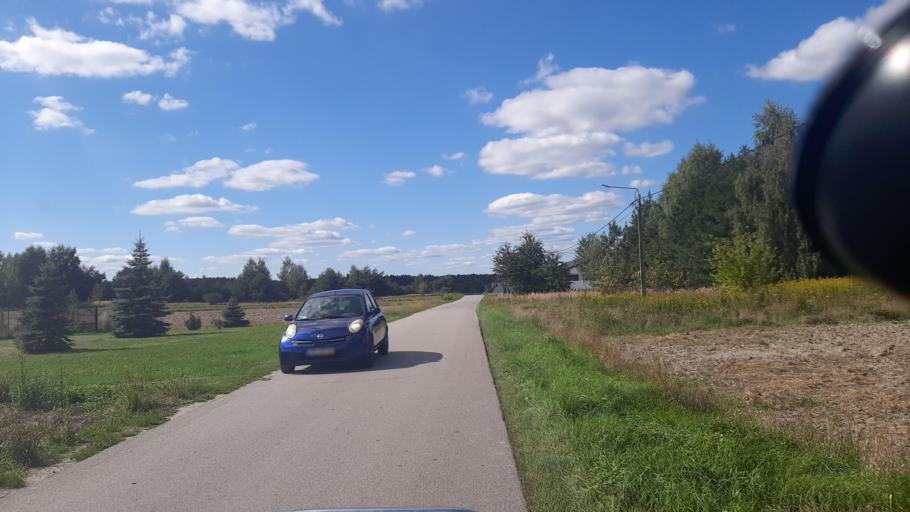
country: PL
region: Lublin Voivodeship
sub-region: Powiat lubelski
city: Garbow
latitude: 51.4075
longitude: 22.3968
